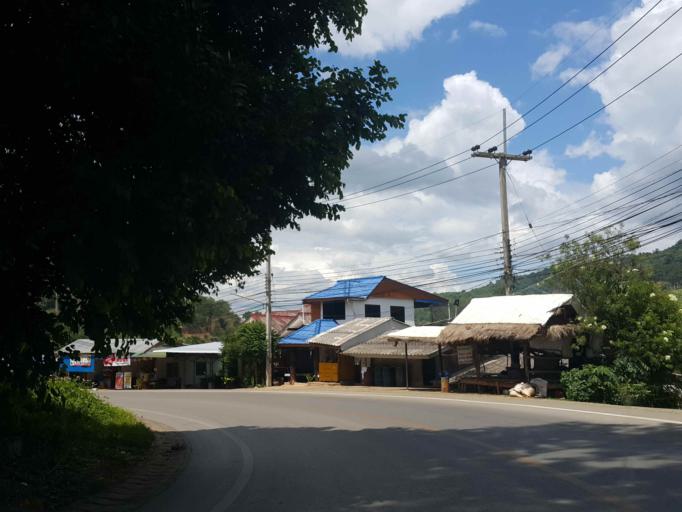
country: TH
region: Chiang Mai
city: Samoeng
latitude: 18.8843
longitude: 98.8203
